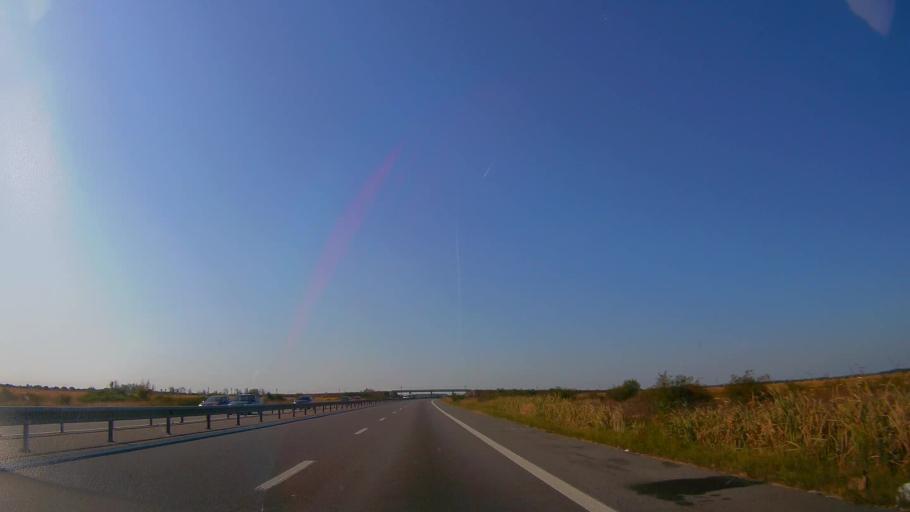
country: RO
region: Dambovita
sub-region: Comuna Corbii Mari
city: Corbii Mari
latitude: 44.5437
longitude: 25.5144
